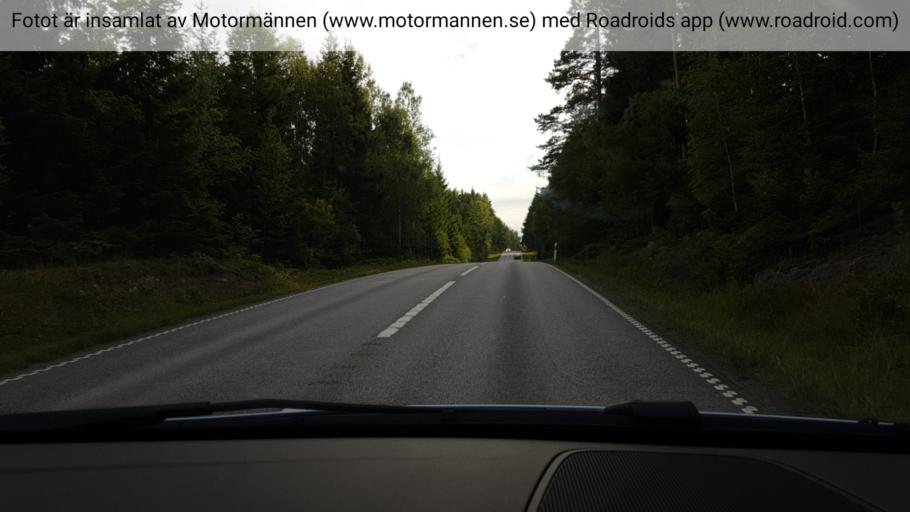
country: SE
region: Stockholm
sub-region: Norrtalje Kommun
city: Norrtalje
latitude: 59.8684
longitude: 18.6950
